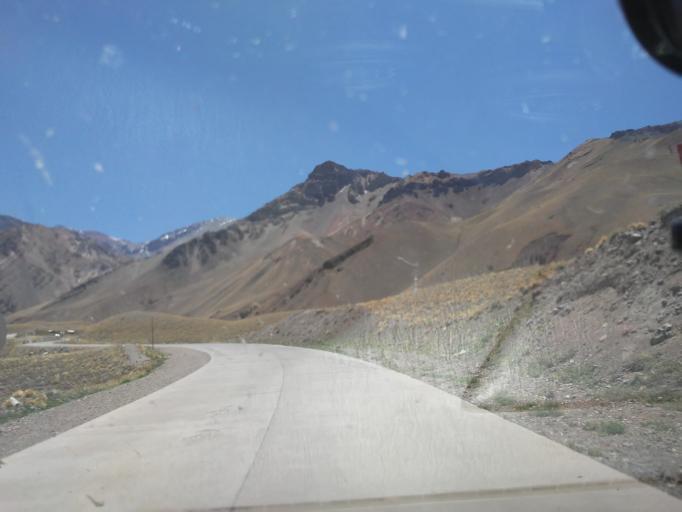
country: CL
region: Valparaiso
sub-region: Provincia de Los Andes
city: Los Andes
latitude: -32.8158
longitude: -69.9423
